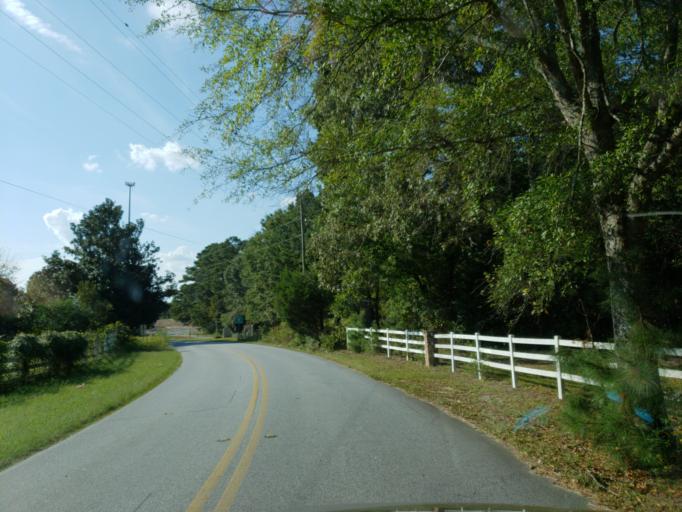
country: US
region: Georgia
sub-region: Paulding County
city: Hiram
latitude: 33.8789
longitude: -84.7239
